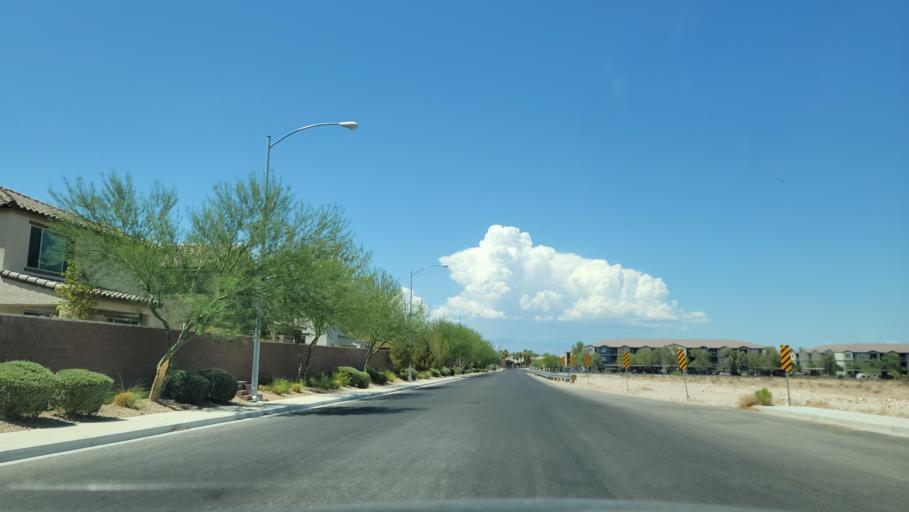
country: US
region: Nevada
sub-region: Clark County
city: Enterprise
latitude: 36.0572
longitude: -115.2656
